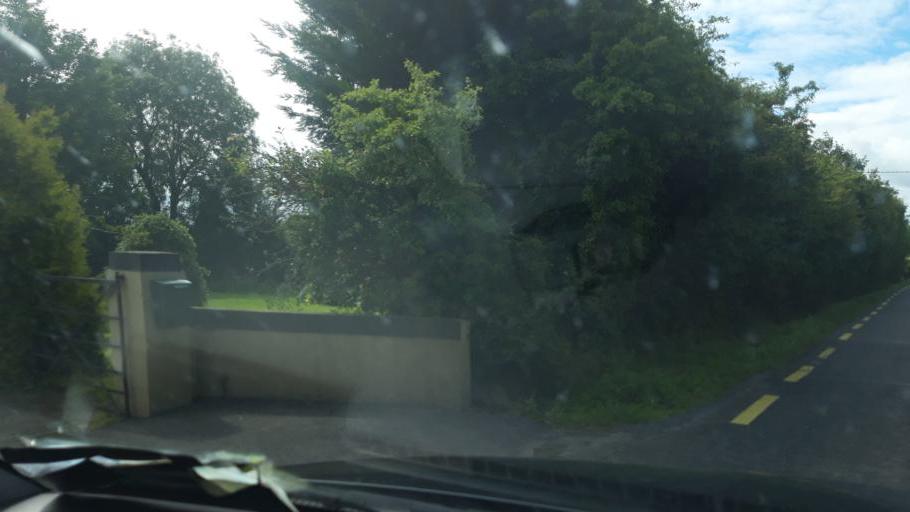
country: IE
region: Leinster
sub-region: Kilkenny
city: Callan
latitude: 52.5251
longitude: -7.4162
